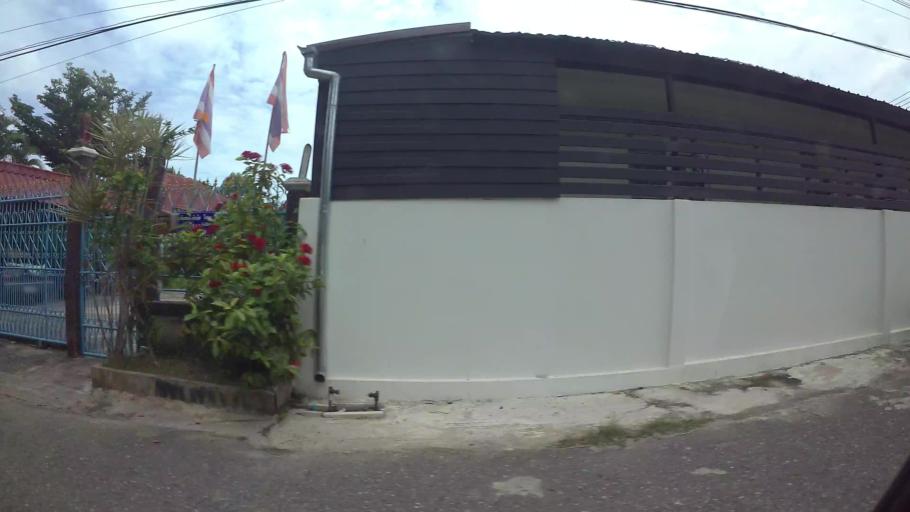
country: TH
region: Chon Buri
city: Sattahip
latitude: 12.6787
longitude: 100.9084
